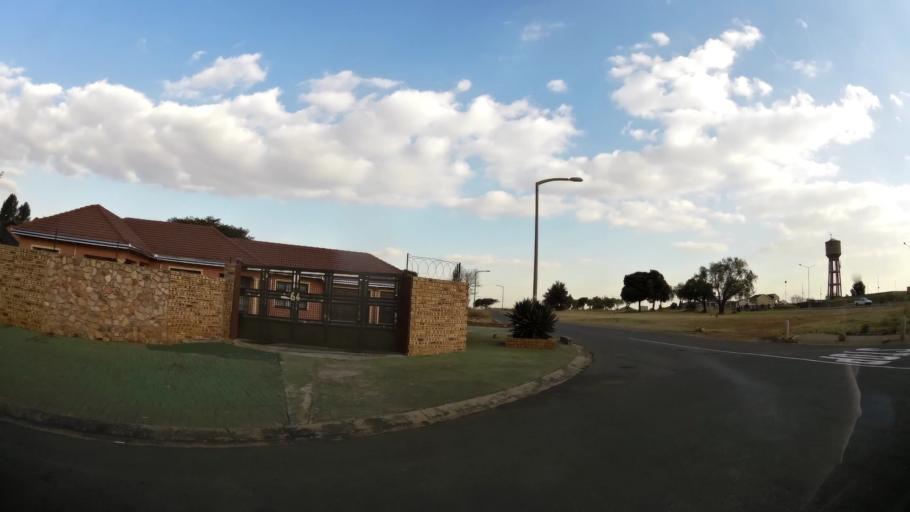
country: ZA
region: Gauteng
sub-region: West Rand District Municipality
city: Krugersdorp
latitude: -26.0722
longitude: 27.7622
